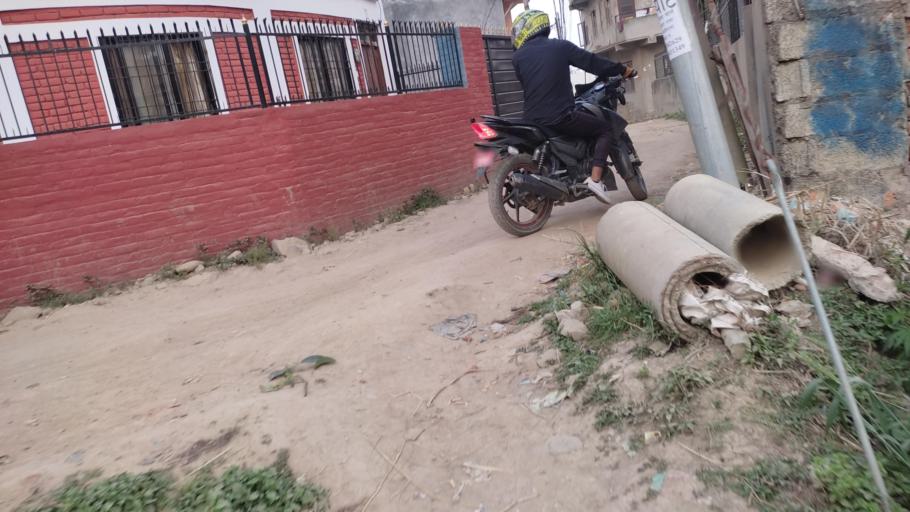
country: NP
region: Central Region
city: Kirtipur
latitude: 27.6712
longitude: 85.2825
